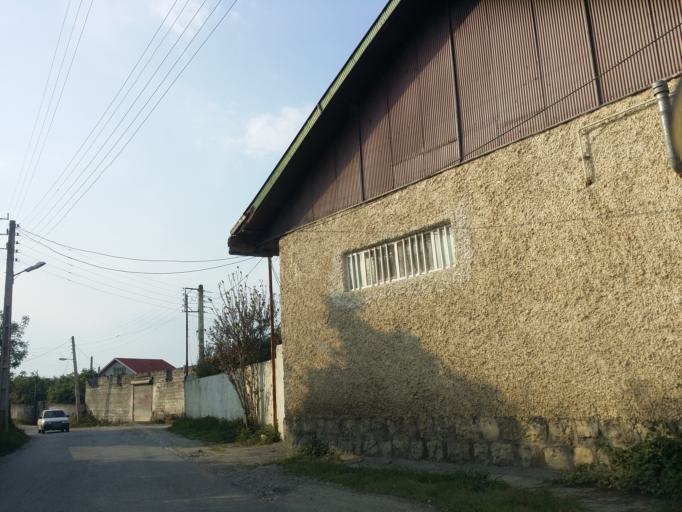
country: IR
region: Mazandaran
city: Chalus
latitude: 36.6650
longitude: 51.3749
